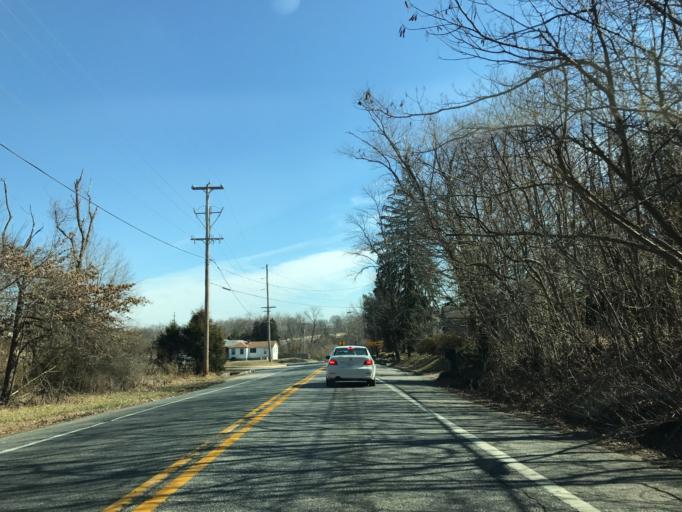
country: US
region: Maryland
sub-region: Cecil County
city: Elkton
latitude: 39.6061
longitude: -75.8551
